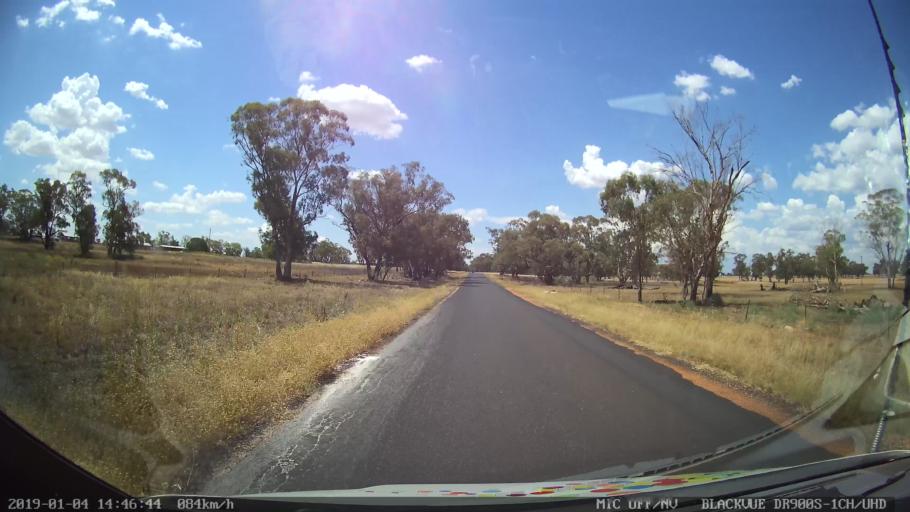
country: AU
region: New South Wales
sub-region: Dubbo Municipality
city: Dubbo
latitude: -32.0777
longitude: 148.6588
